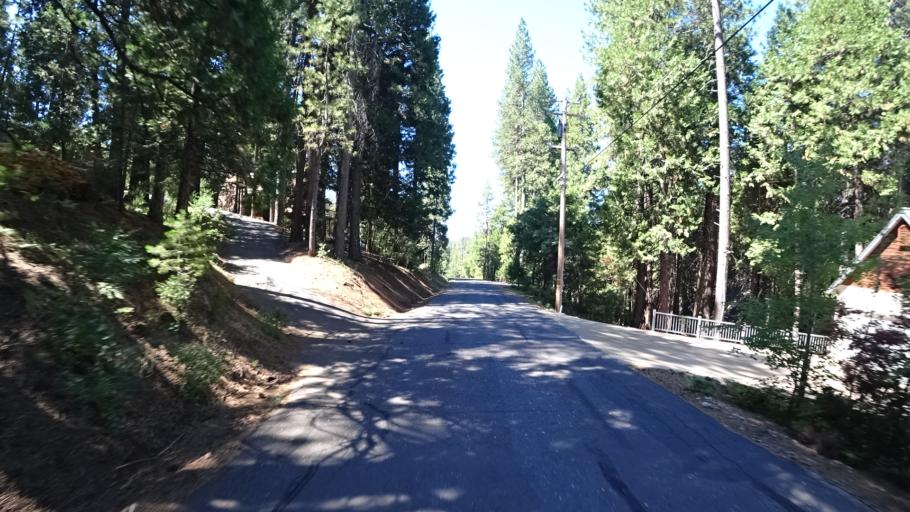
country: US
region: California
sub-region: Calaveras County
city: Arnold
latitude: 38.2400
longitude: -120.3740
